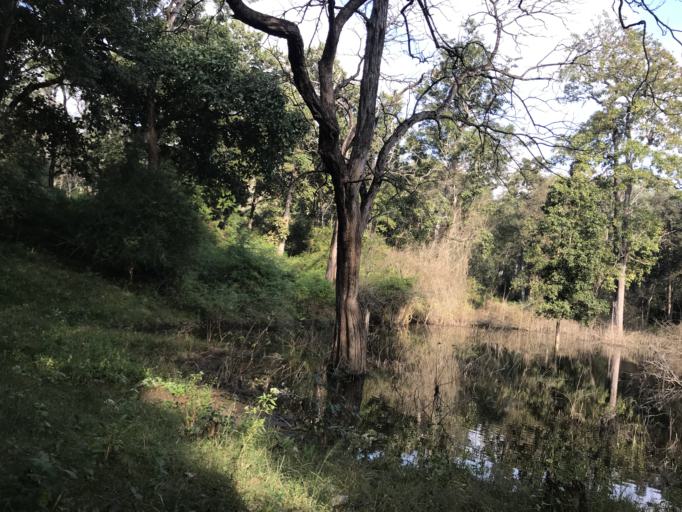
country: IN
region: Karnataka
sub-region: Mysore
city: Heggadadevankote
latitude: 11.9533
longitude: 76.1955
